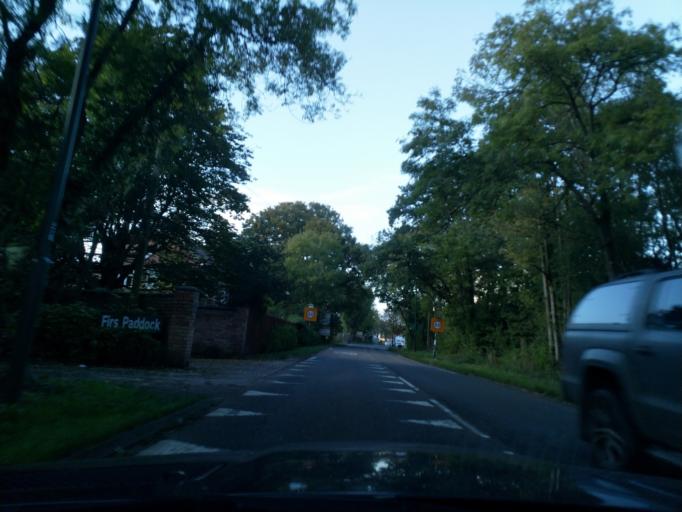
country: GB
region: England
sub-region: Solihull
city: Cheswick Green
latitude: 52.3479
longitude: -1.7770
